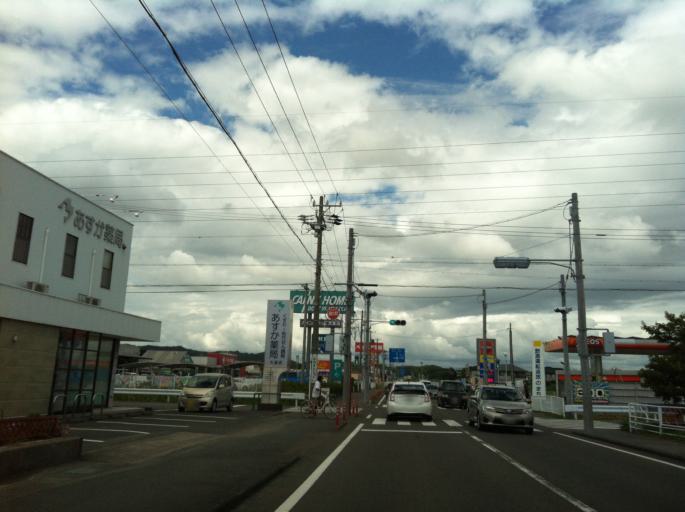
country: JP
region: Shizuoka
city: Kakegawa
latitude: 34.6715
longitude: 138.0453
